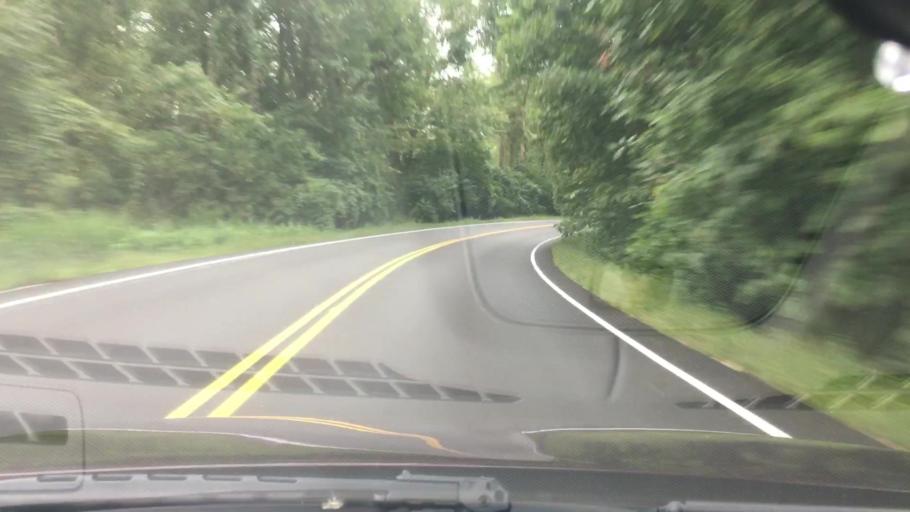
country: US
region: New York
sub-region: Dutchess County
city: Dover Plains
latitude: 41.8603
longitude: -73.5106
